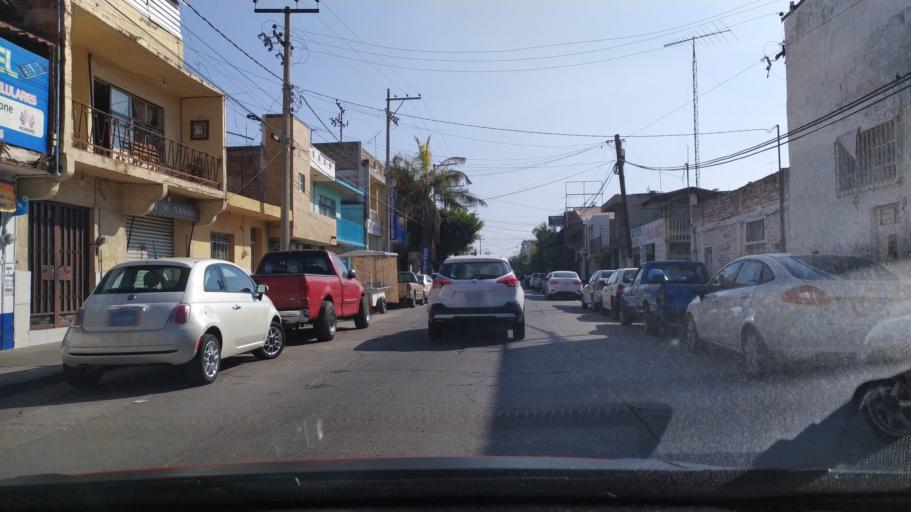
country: MX
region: Guanajuato
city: San Francisco del Rincon
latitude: 21.0155
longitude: -101.8567
